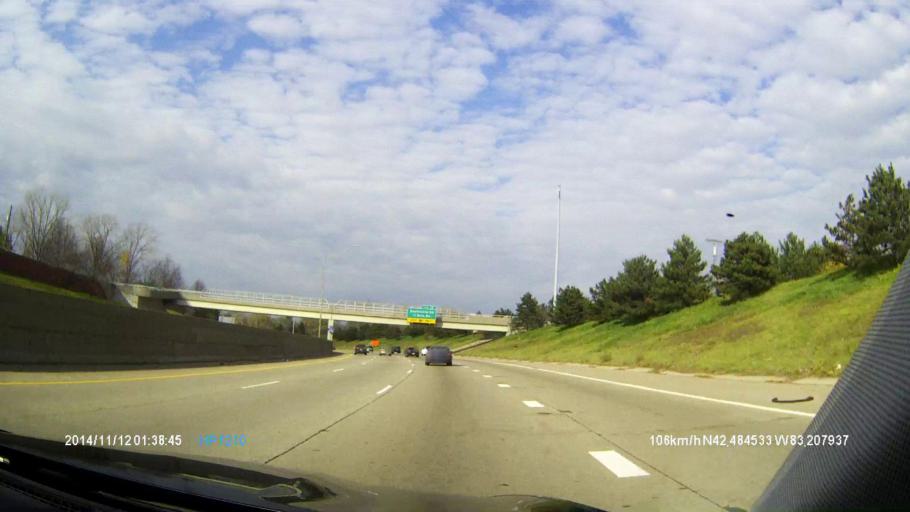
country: US
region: Michigan
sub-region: Oakland County
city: Southfield
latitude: 42.4848
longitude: -83.2081
